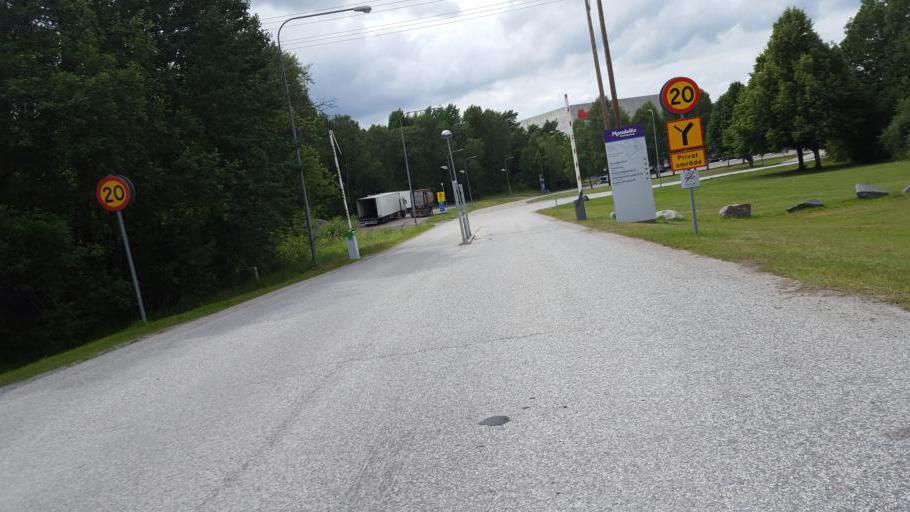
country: SE
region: Stockholm
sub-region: Upplands Vasby Kommun
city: Upplands Vaesby
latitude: 59.5069
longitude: 17.9013
